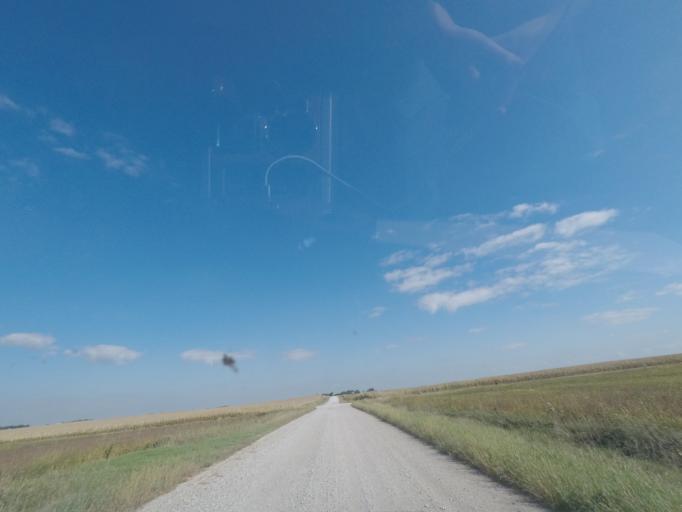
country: US
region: Iowa
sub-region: Story County
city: Nevada
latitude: 42.0482
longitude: -93.4252
